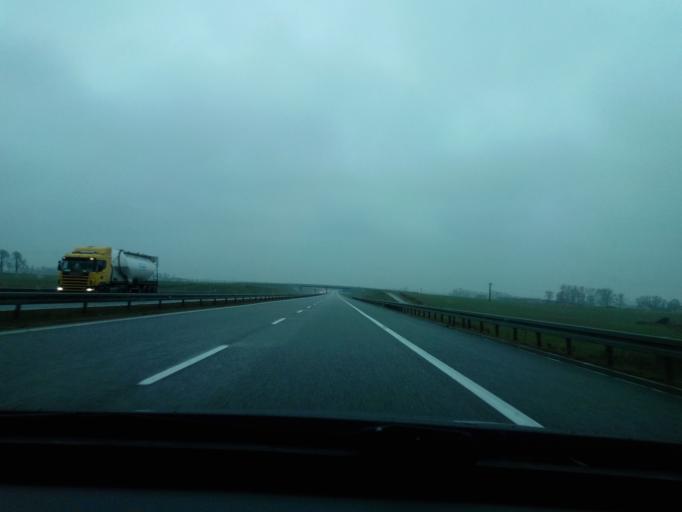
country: PL
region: Pomeranian Voivodeship
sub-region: Powiat gdanski
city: Pszczolki
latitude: 54.0885
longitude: 18.6918
